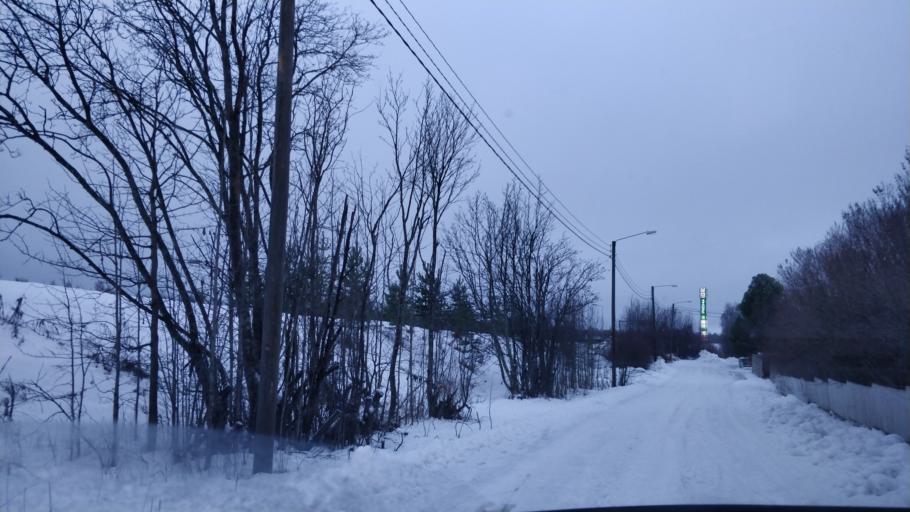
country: FI
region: Lapland
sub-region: Kemi-Tornio
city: Kemi
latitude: 65.7462
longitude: 24.5786
